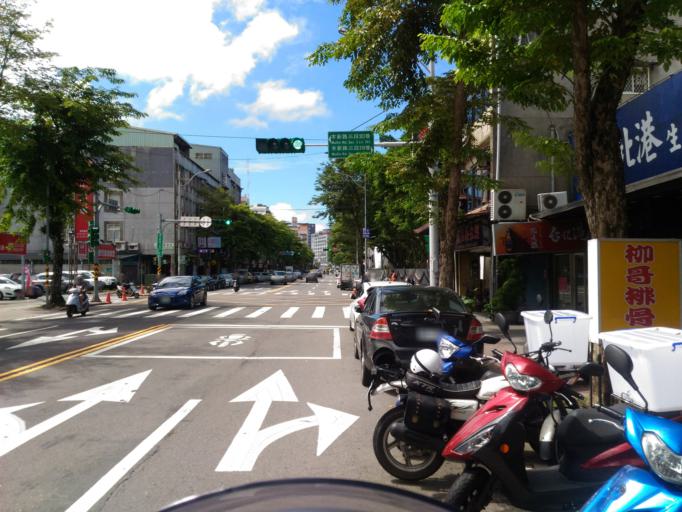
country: TW
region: Taipei
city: Taipei
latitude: 24.9810
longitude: 121.5575
